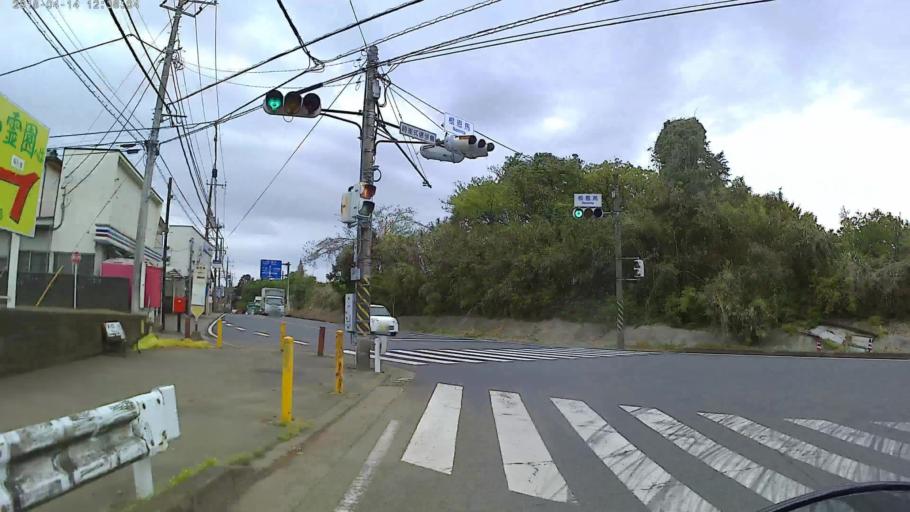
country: JP
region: Kanagawa
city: Atsugi
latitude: 35.4113
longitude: 139.4064
